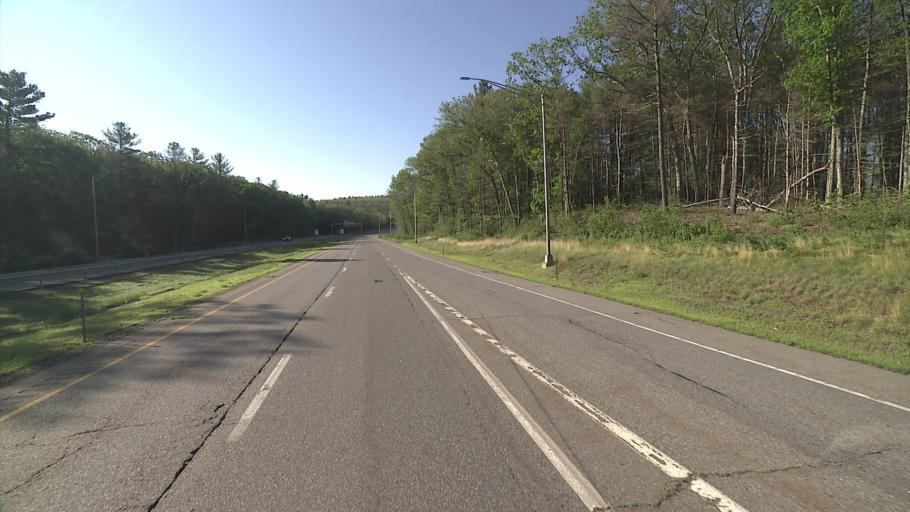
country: US
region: Connecticut
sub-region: Windham County
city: Danielson
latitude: 41.7896
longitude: -71.8755
